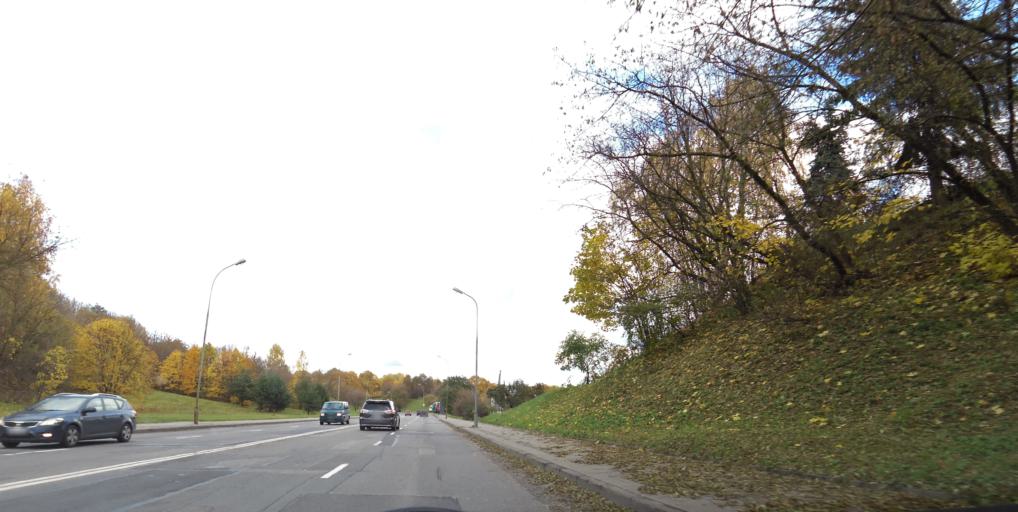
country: LT
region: Vilnius County
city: Rasos
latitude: 54.6638
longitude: 25.3035
